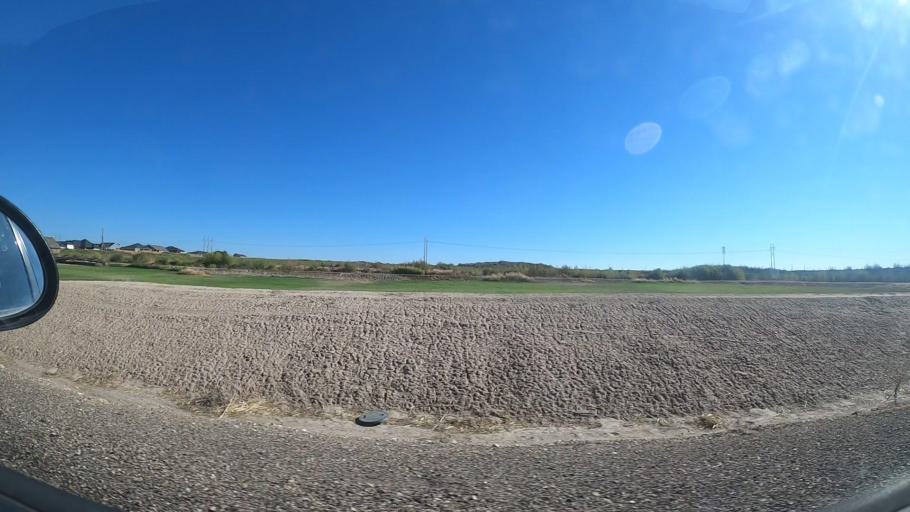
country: US
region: Idaho
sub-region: Canyon County
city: Nampa
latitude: 43.5472
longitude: -116.6097
